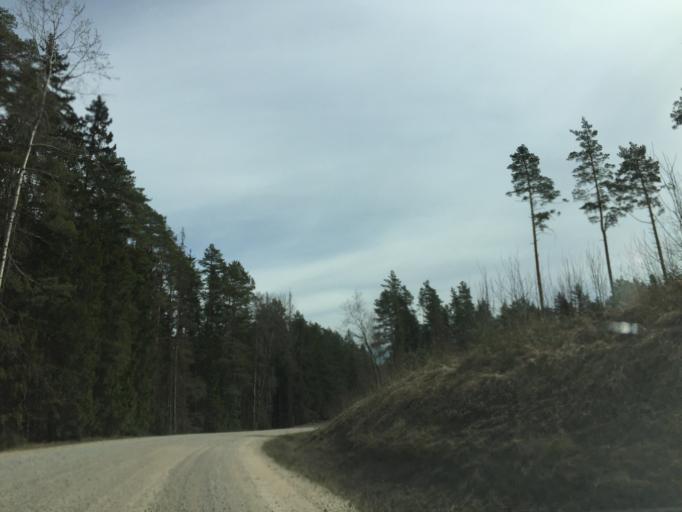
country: LV
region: Valkas Rajons
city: Valka
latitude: 57.7989
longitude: 25.9601
